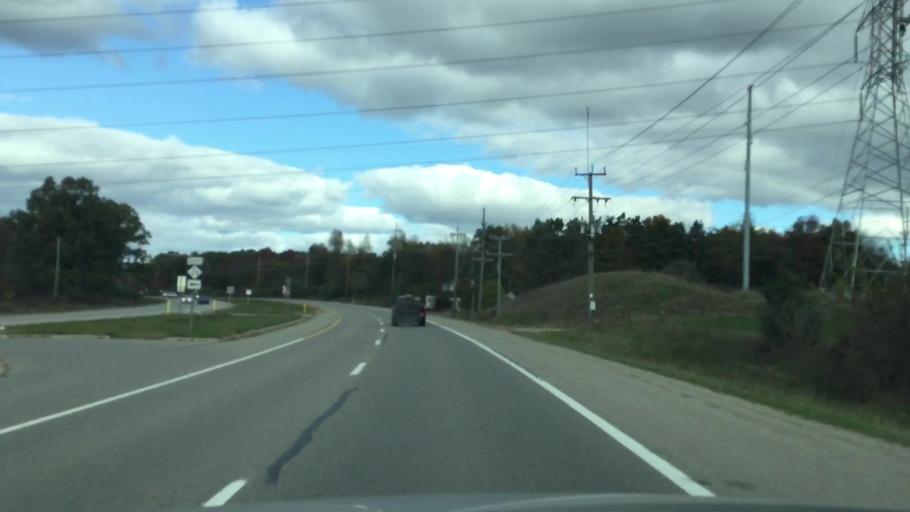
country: US
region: Michigan
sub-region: Lapeer County
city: Lapeer
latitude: 42.9879
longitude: -83.3153
